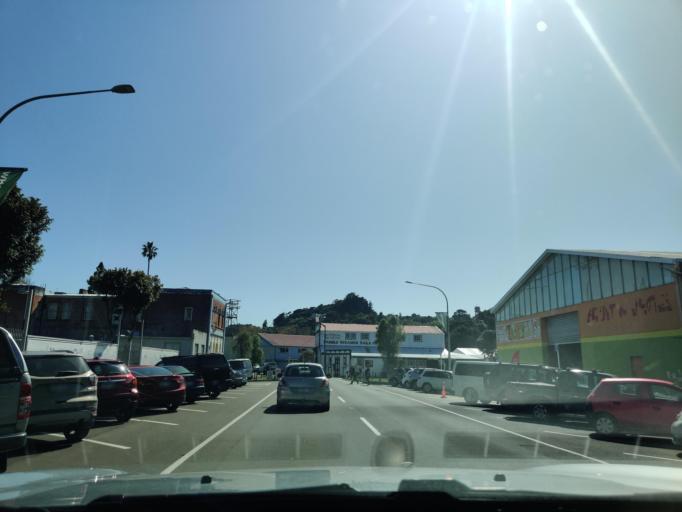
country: NZ
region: Manawatu-Wanganui
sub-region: Wanganui District
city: Wanganui
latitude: -39.9334
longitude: 175.0569
